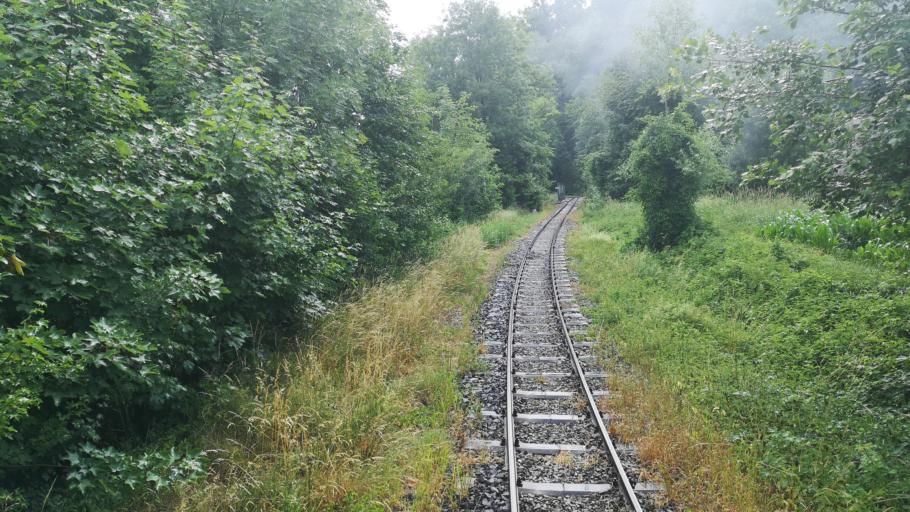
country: AT
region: Upper Austria
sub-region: Politischer Bezirk Steyr-Land
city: Garsten
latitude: 48.0400
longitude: 14.3960
